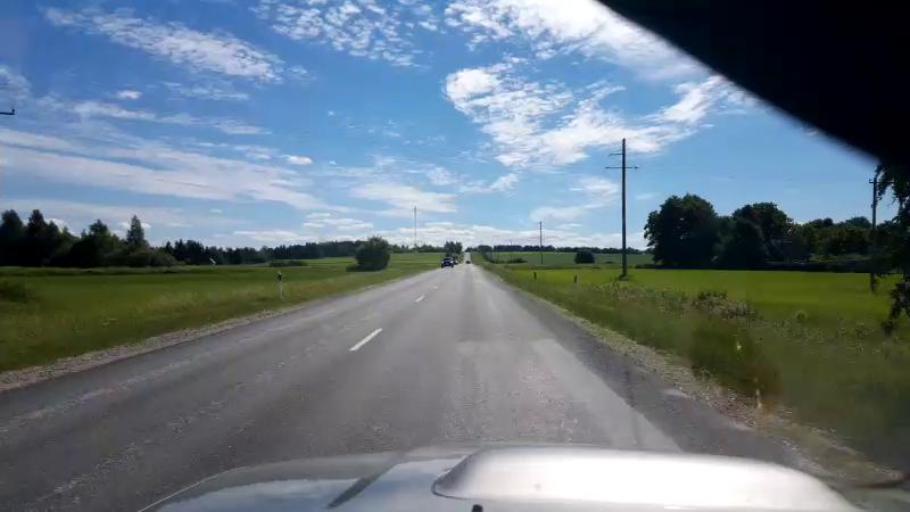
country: EE
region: Laeaene-Virumaa
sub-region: Rakke vald
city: Rakke
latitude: 58.8598
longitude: 26.2931
